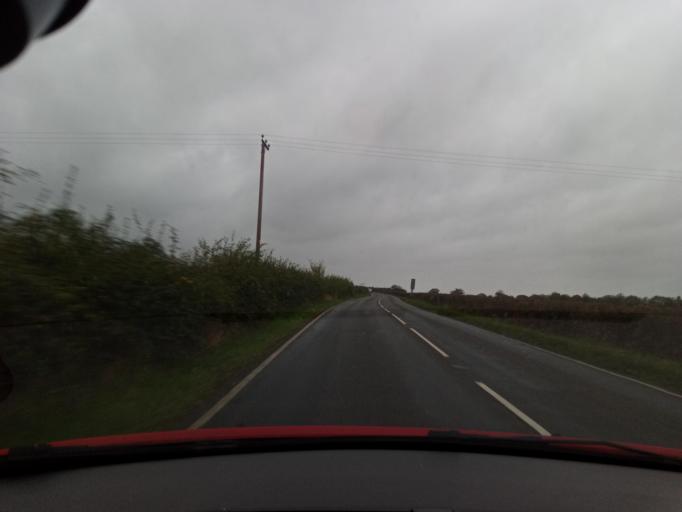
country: GB
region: England
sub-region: Essex
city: Great Yeldham
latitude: 52.0415
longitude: 0.5277
